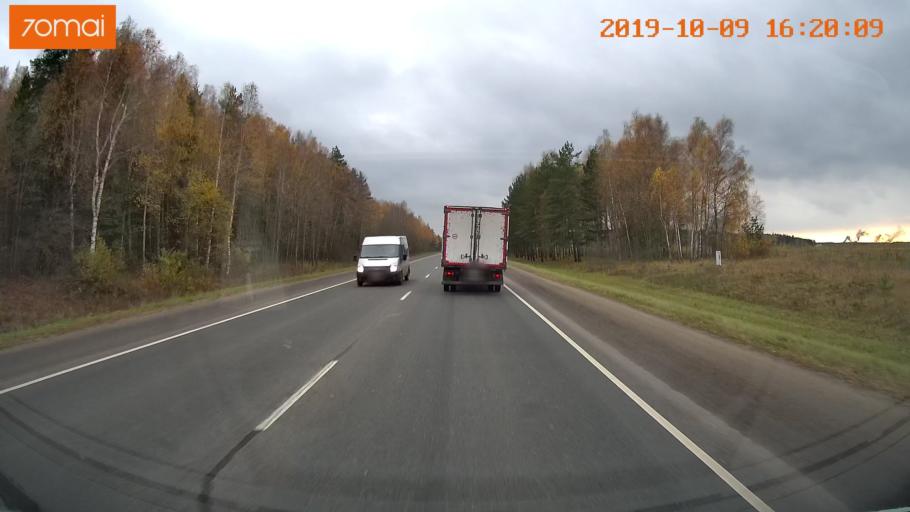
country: RU
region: Kostroma
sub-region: Kostromskoy Rayon
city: Kostroma
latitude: 57.7100
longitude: 40.8929
